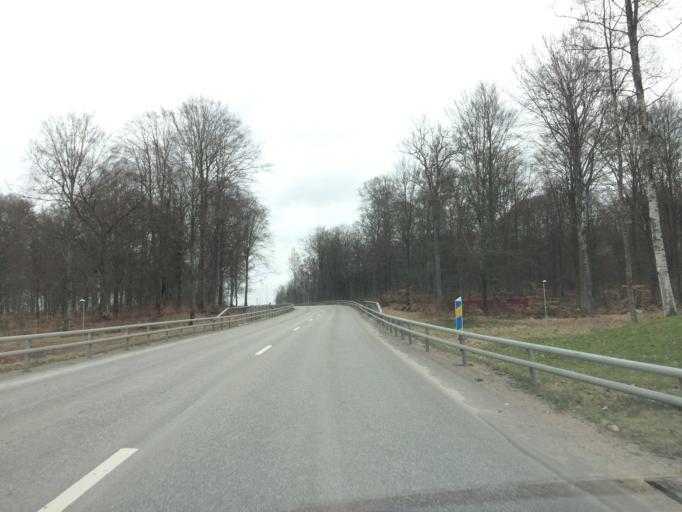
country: SE
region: Kronoberg
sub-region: Almhults Kommun
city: AElmhult
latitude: 56.5494
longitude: 14.1449
